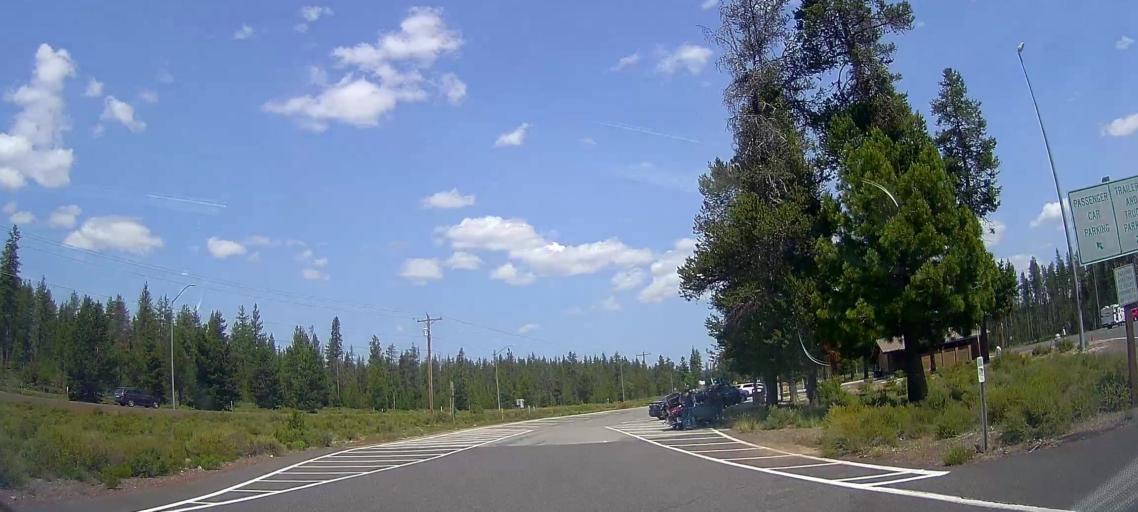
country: US
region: Oregon
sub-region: Deschutes County
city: La Pine
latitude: 43.1719
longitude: -121.7867
